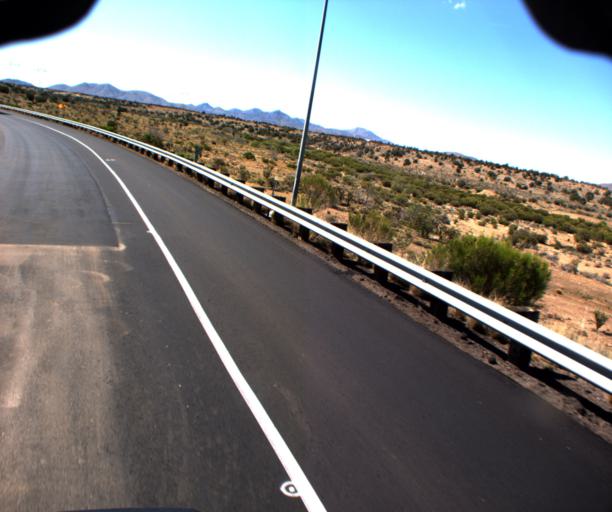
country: US
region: Arizona
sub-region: Mohave County
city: New Kingman-Butler
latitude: 35.1609
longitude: -113.6977
